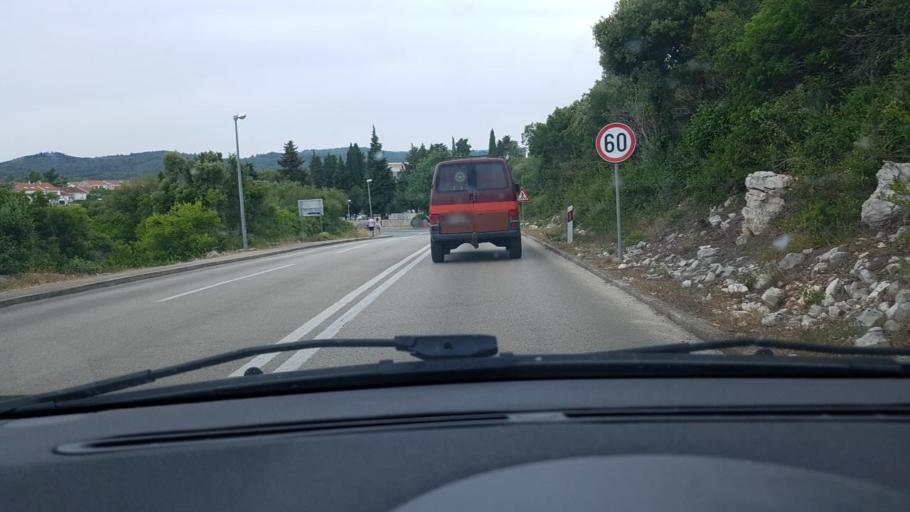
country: HR
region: Dubrovacko-Neretvanska
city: Korcula
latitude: 42.9524
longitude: 17.1476
